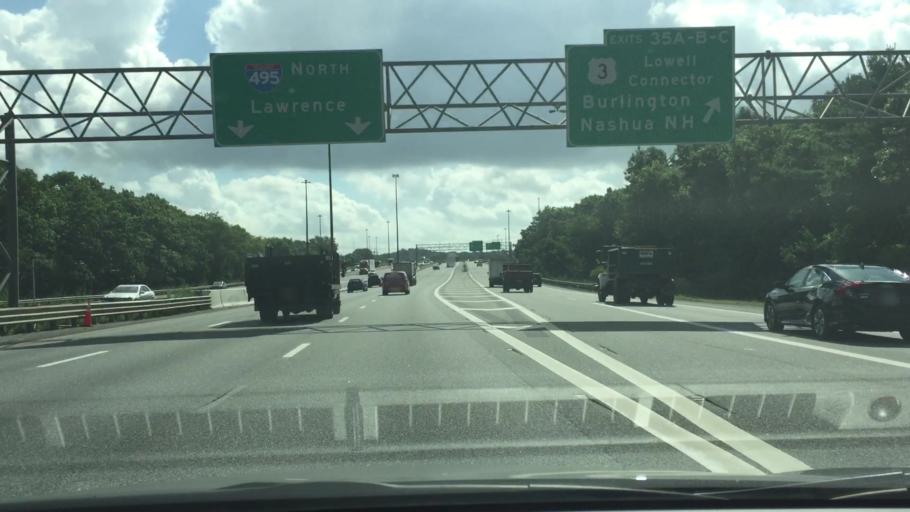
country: US
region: Massachusetts
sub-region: Middlesex County
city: Lowell
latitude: 42.6068
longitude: -71.3351
